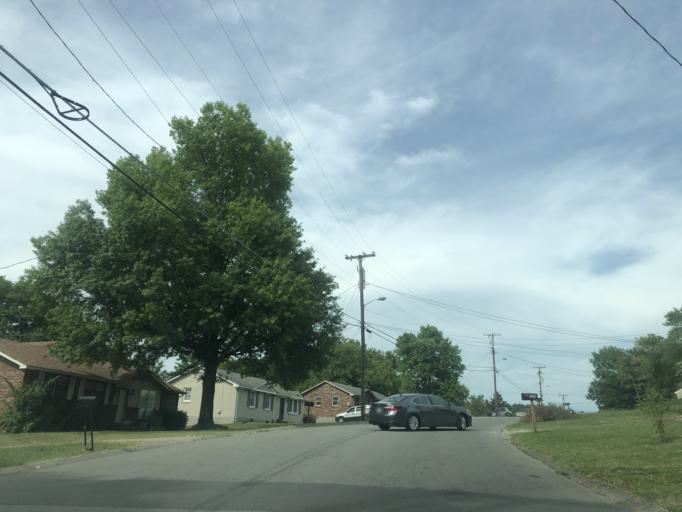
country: US
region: Tennessee
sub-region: Davidson County
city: Nashville
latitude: 36.2224
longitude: -86.8081
